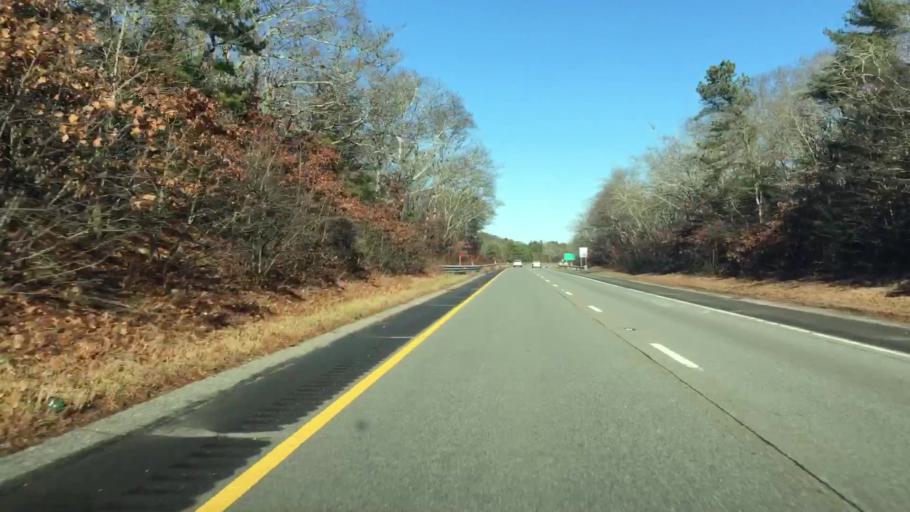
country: US
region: Massachusetts
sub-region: Barnstable County
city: West Falmouth
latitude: 41.6007
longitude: -70.6270
